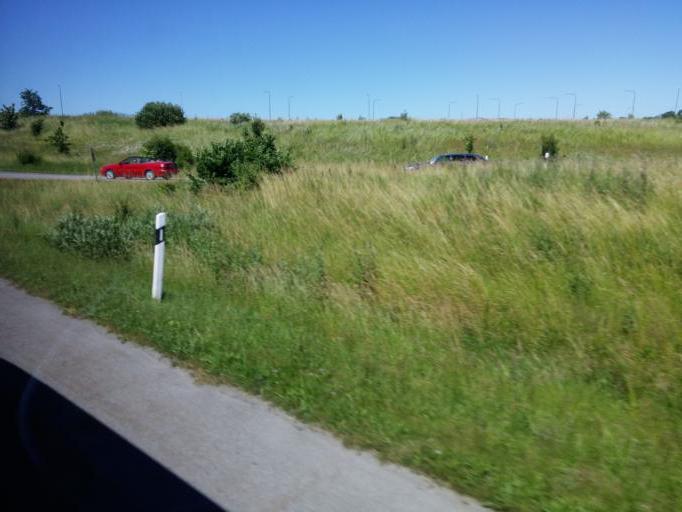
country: SE
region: Skane
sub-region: Malmo
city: Oxie
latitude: 55.5547
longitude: 13.1039
